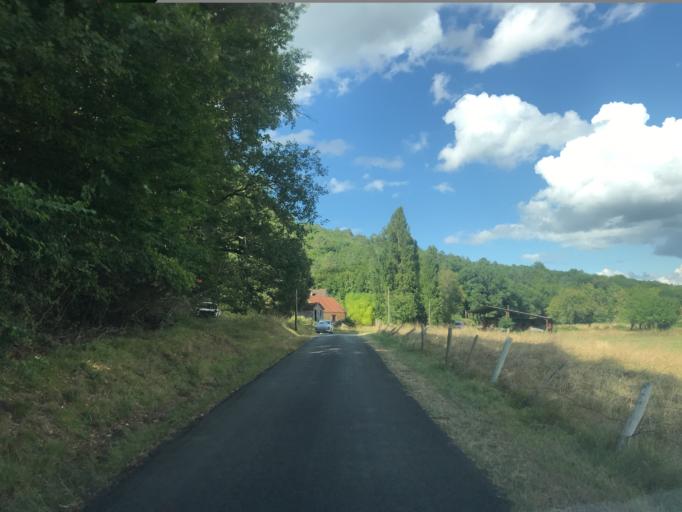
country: FR
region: Aquitaine
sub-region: Departement de la Dordogne
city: Rouffignac-Saint-Cernin-de-Reilhac
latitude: 44.9767
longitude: 1.0352
